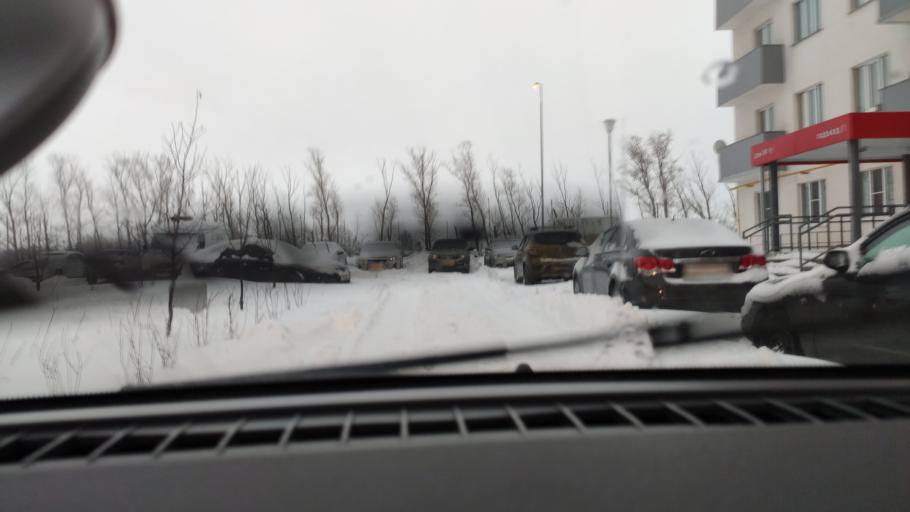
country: RU
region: Samara
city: Samara
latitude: 53.0919
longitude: 50.1610
